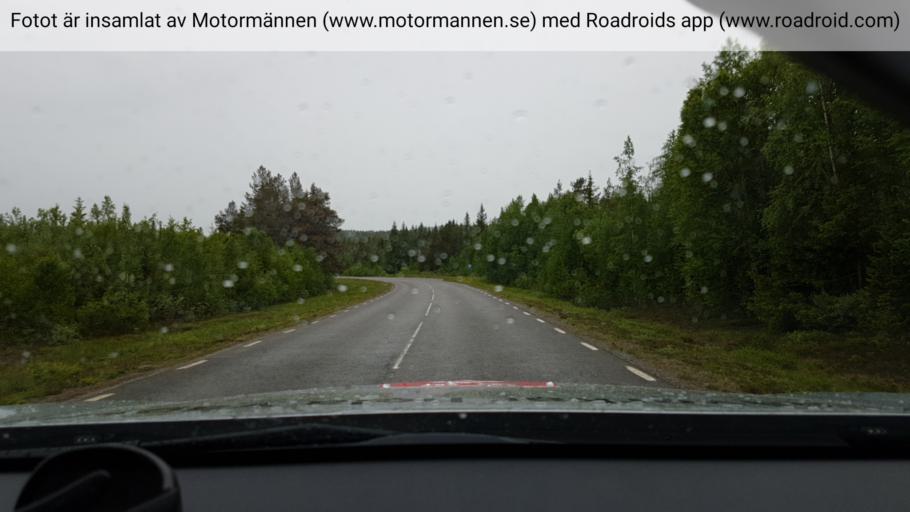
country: SE
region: Vaesterbotten
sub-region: Storumans Kommun
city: Fristad
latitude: 65.8212
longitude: 16.7075
